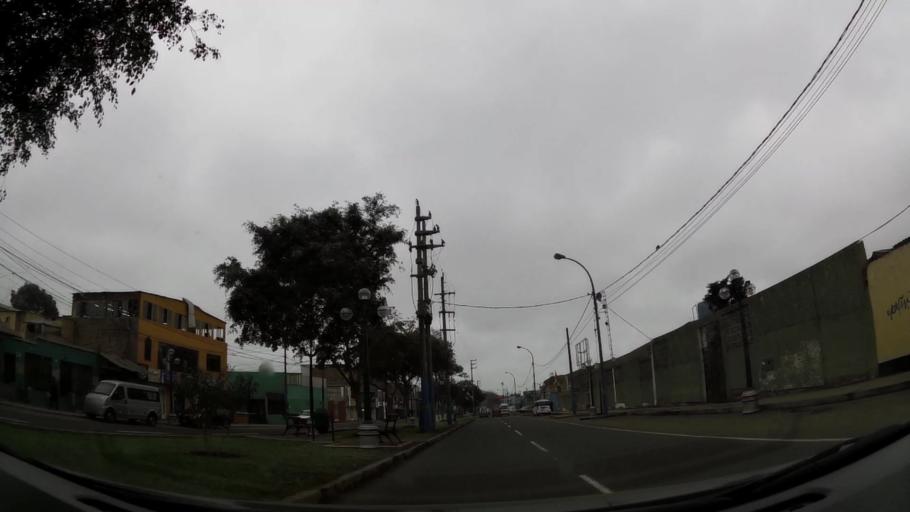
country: PE
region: Lima
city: Ventanilla
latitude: -11.8718
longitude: -77.1228
